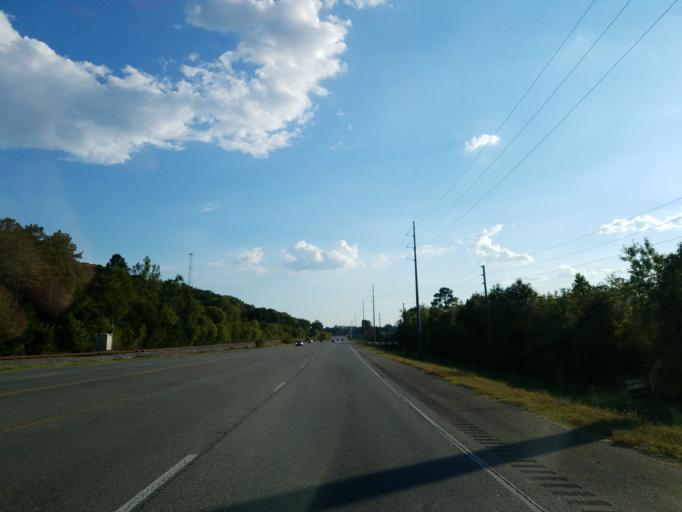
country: US
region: Georgia
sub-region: Murray County
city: Chatsworth
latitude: 34.8102
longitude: -84.7668
